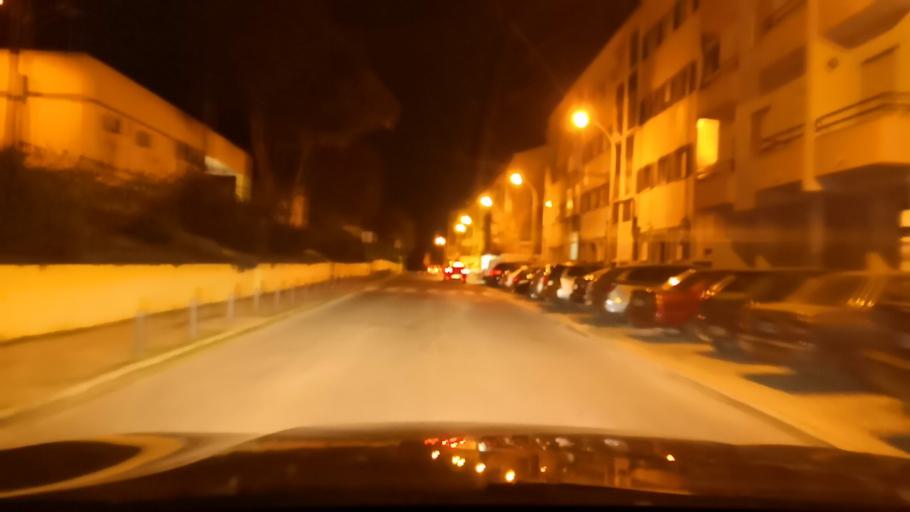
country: PT
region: Setubal
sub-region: Setubal
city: Setubal
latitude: 38.5252
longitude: -8.9061
